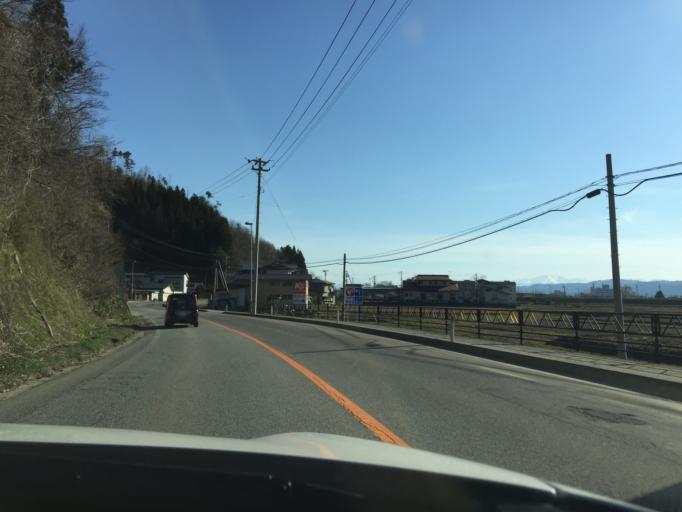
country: JP
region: Yamagata
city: Nagai
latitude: 38.1182
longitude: 140.0513
